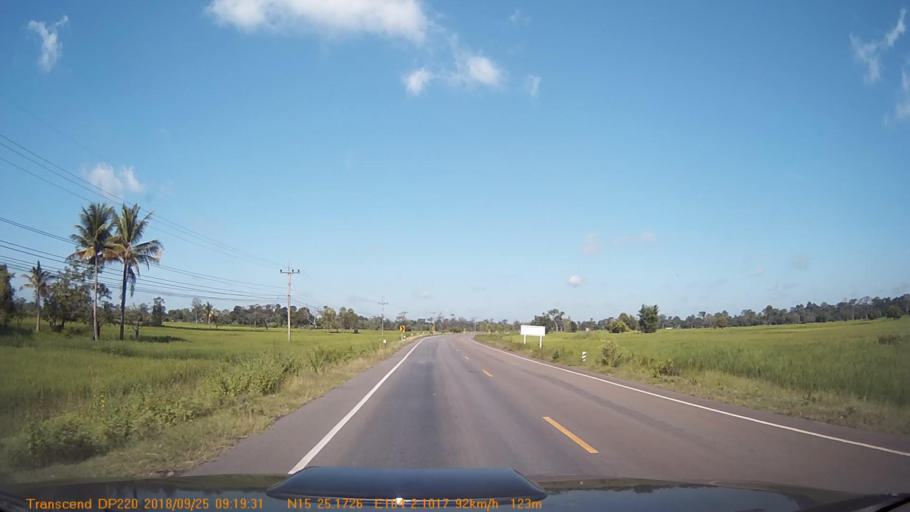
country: TH
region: Sisaket
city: Sila Lat
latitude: 15.4195
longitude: 104.0352
